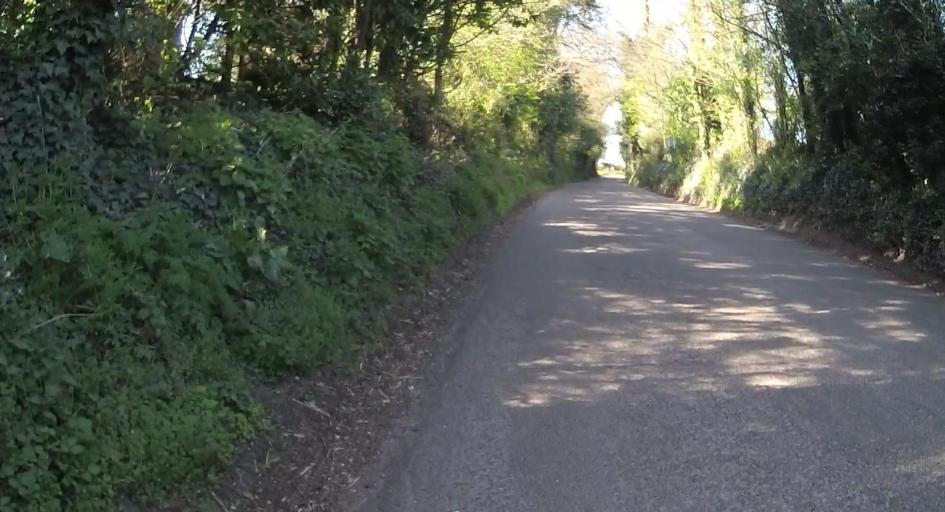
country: GB
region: England
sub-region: Hampshire
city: Abbotts Ann
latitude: 51.1364
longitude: -1.4854
